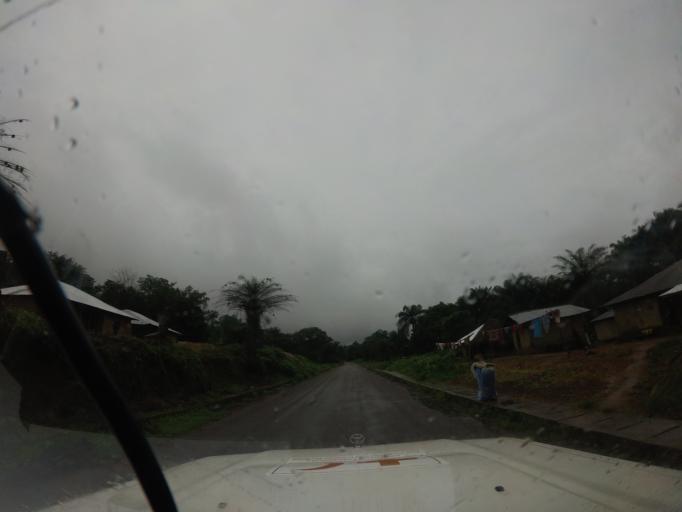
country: SL
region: Northern Province
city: Bumbuna
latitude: 9.3048
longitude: -11.9459
